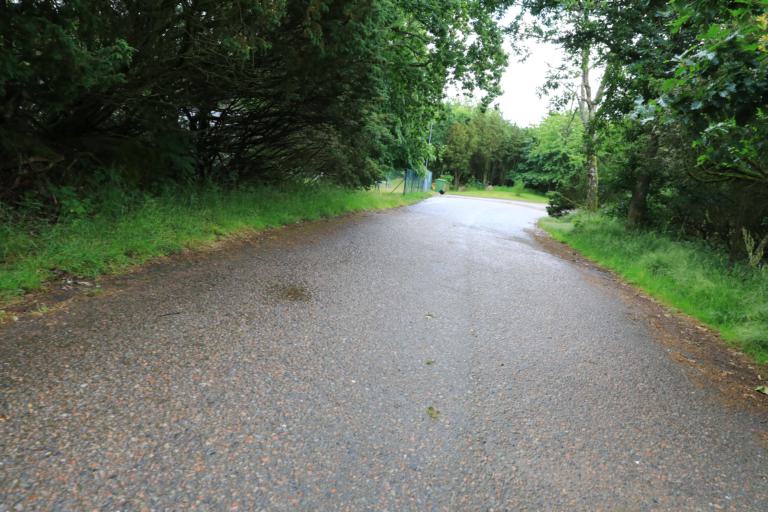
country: SE
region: Halland
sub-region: Varbergs Kommun
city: Varberg
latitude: 57.1724
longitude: 12.2897
